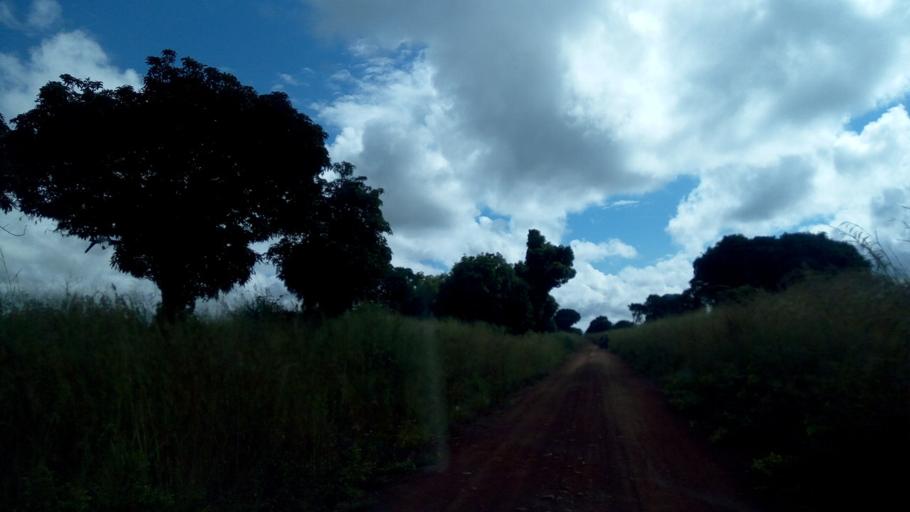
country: ZM
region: Northern
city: Kaputa
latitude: -8.4274
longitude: 28.9254
